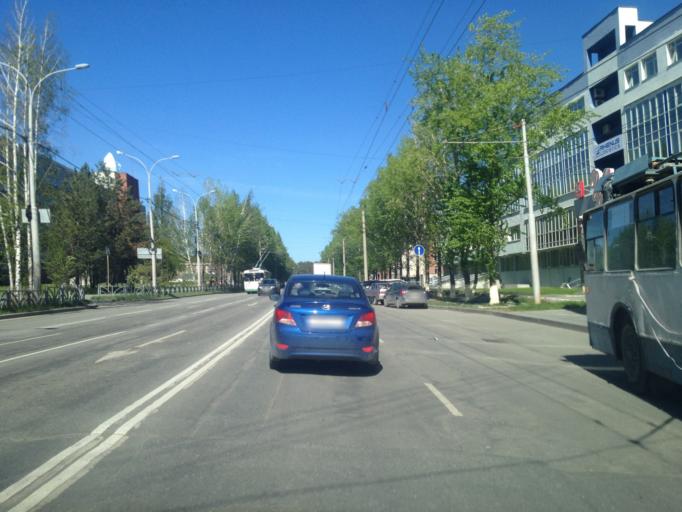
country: RU
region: Sverdlovsk
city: Sovkhoznyy
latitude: 56.7765
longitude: 60.5525
